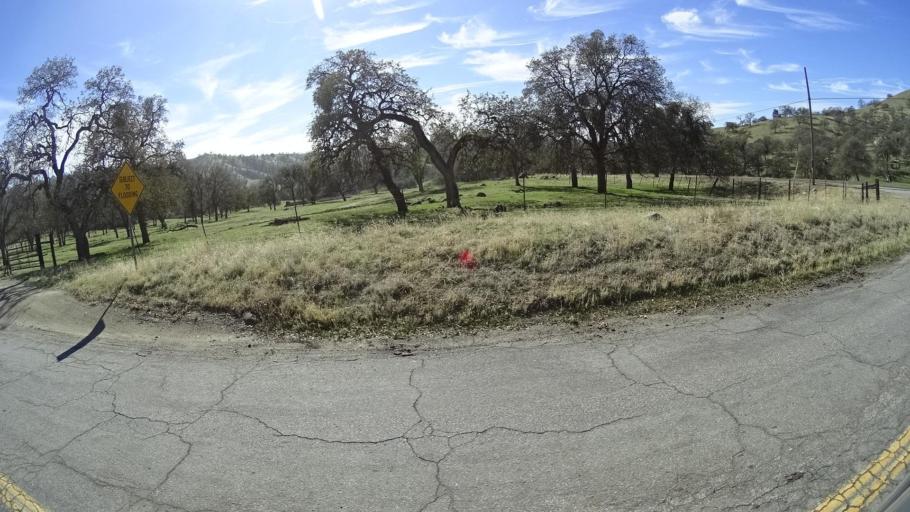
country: US
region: California
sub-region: Kern County
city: Alta Sierra
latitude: 35.6305
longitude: -118.7992
